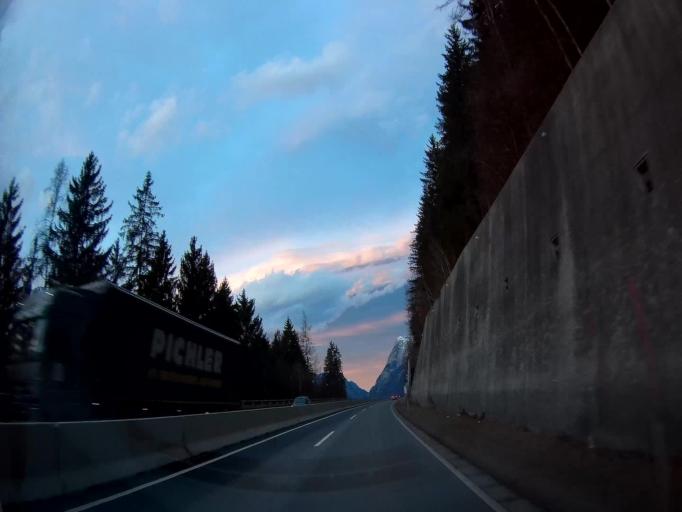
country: AT
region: Salzburg
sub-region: Politischer Bezirk Sankt Johann im Pongau
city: Bischofshofen
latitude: 47.4093
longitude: 13.2241
